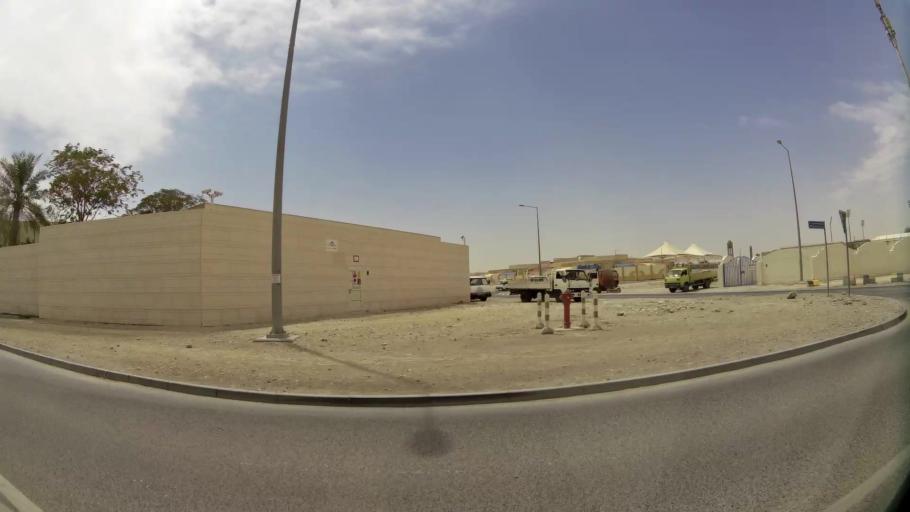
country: QA
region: Baladiyat ar Rayyan
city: Ar Rayyan
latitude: 25.2819
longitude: 51.4352
